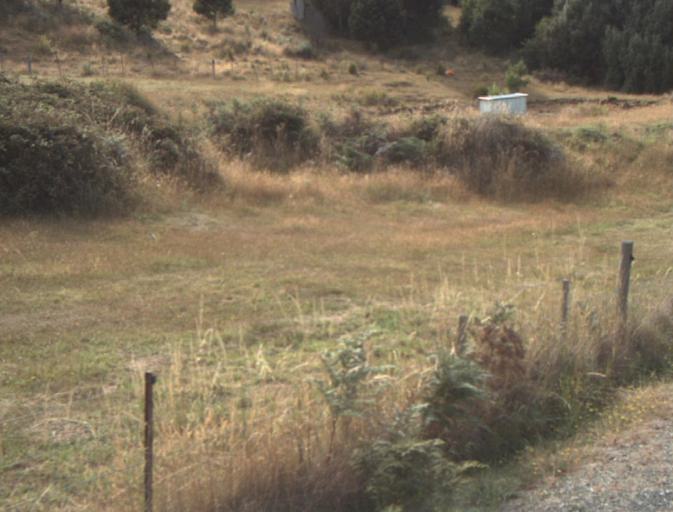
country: AU
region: Tasmania
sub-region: Launceston
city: Mayfield
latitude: -41.2826
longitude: 147.1963
